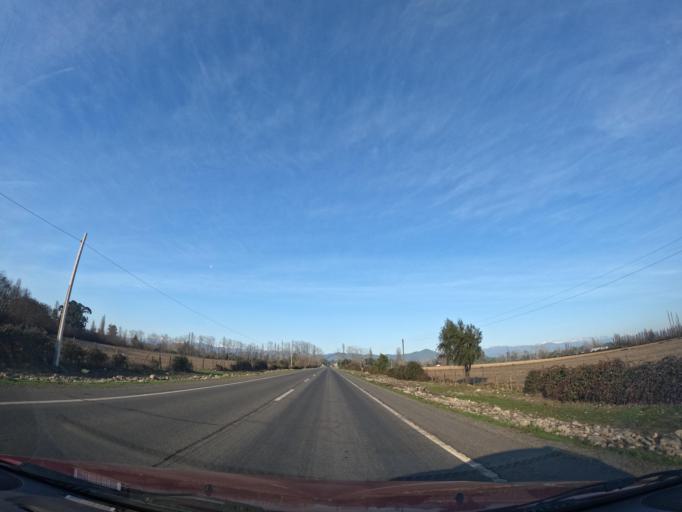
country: CL
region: Maule
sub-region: Provincia de Linares
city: Colbun
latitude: -35.6304
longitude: -71.4392
